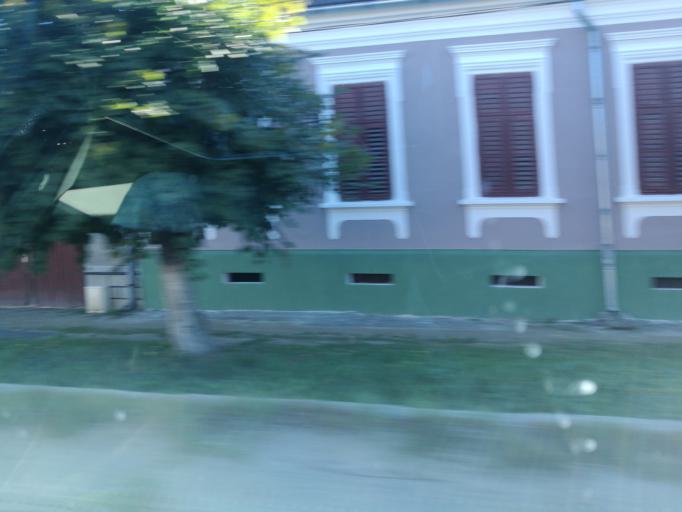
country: RO
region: Brasov
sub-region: Comuna Sercaia
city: Sercaia
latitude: 45.8301
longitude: 25.1437
